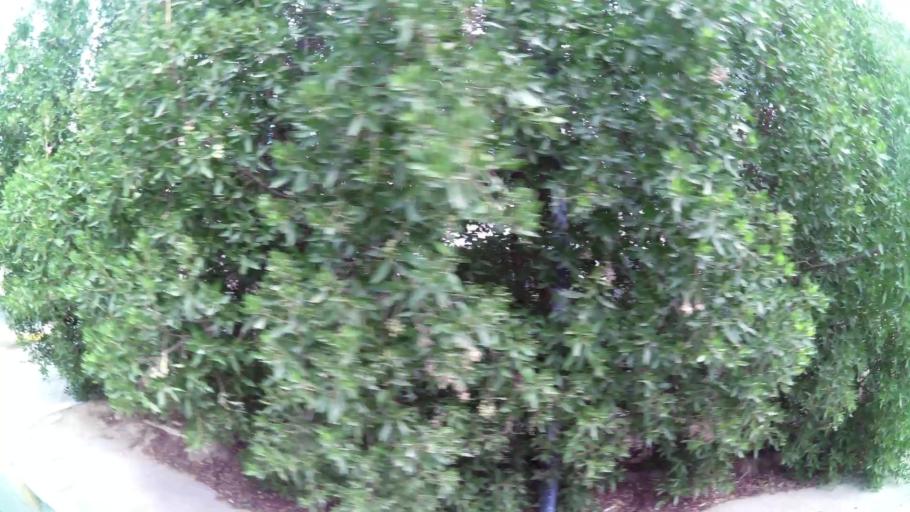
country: AE
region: Abu Dhabi
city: Al Ain
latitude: 24.2251
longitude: 55.7538
